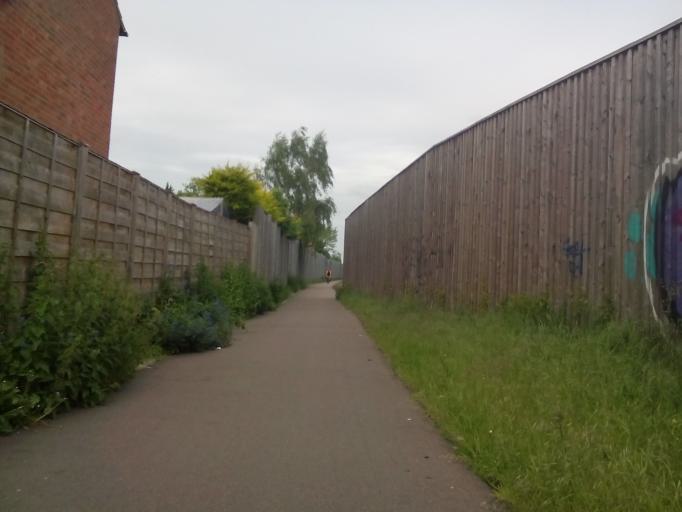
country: GB
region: England
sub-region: Cambridgeshire
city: Histon
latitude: 52.2425
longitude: 0.1094
